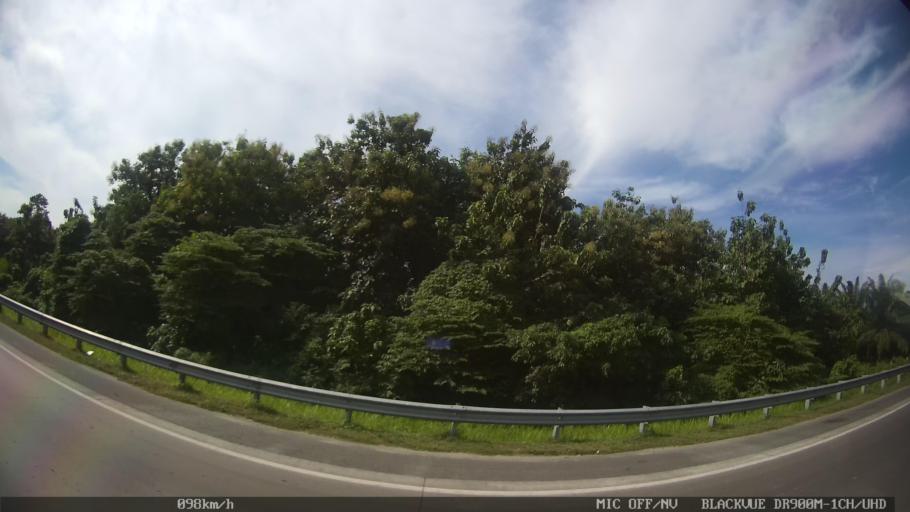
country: ID
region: North Sumatra
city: Sunggal
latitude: 3.6384
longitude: 98.6113
